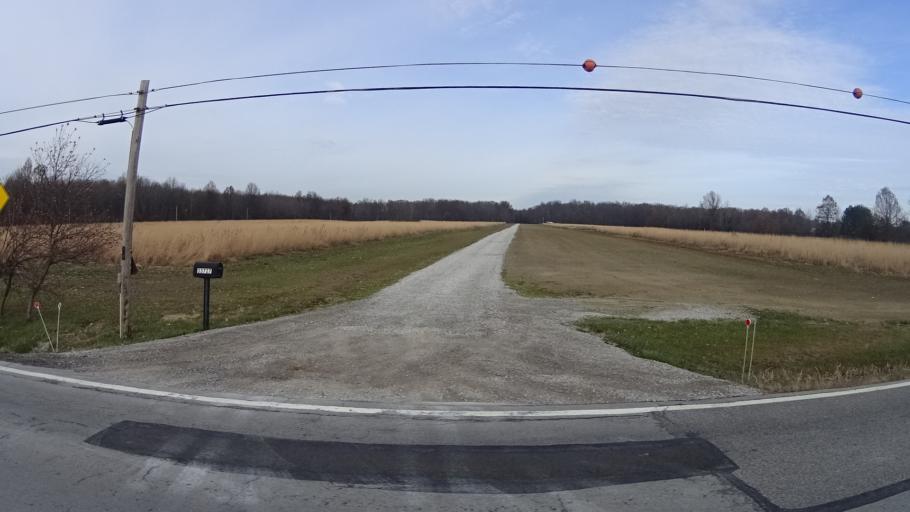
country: US
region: Ohio
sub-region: Lorain County
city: Eaton Estates
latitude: 41.2374
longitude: -81.9783
